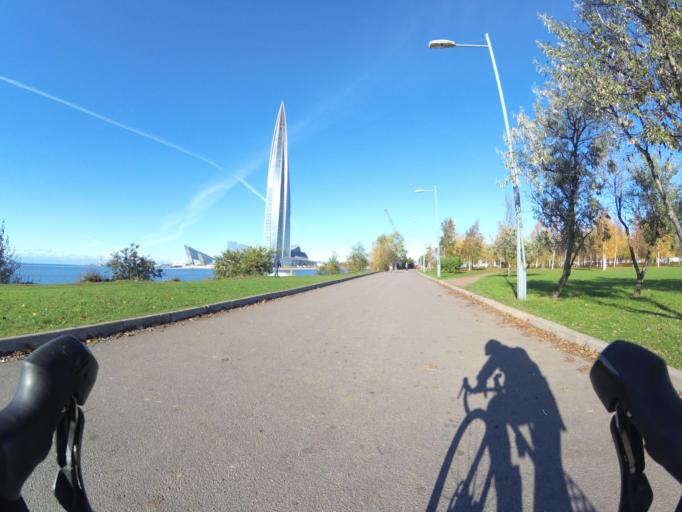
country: RU
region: Leningrad
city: Untolovo
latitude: 59.9836
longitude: 30.1898
